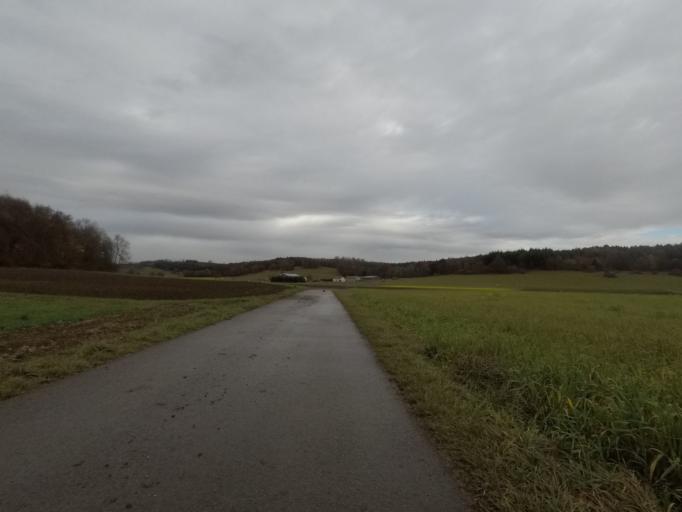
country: DE
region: Baden-Wuerttemberg
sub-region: Tuebingen Region
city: Sankt Johann
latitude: 48.4038
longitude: 9.2836
